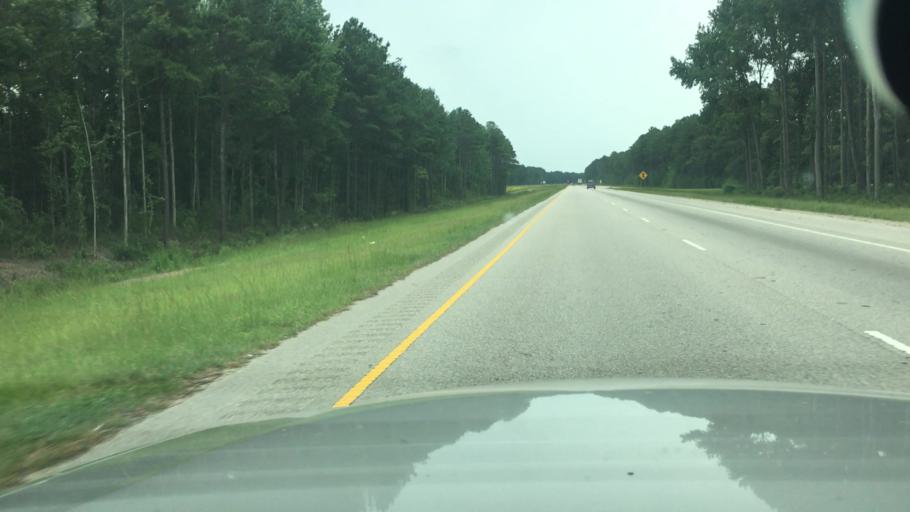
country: US
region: North Carolina
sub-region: Cumberland County
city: Fayetteville
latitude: 34.9747
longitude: -78.8556
